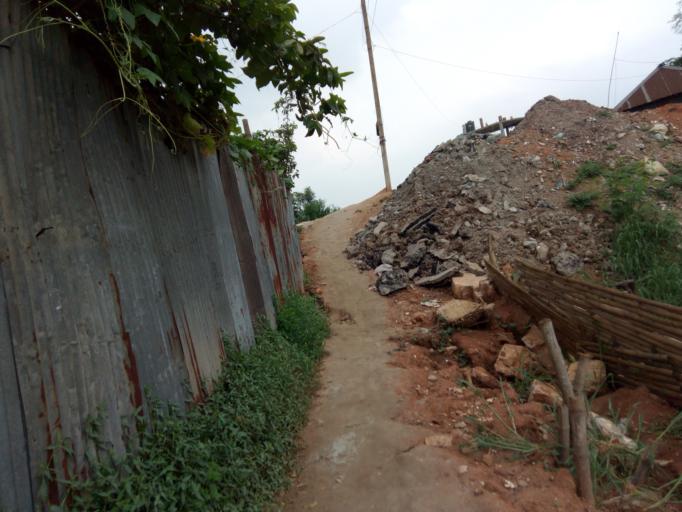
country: BD
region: Dhaka
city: Paltan
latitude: 23.7514
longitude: 90.4533
